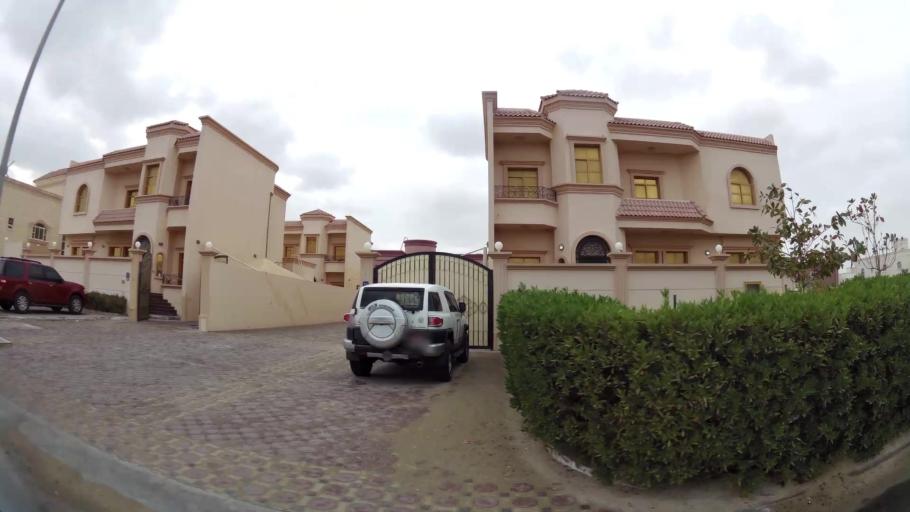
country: AE
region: Abu Dhabi
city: Abu Dhabi
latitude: 24.3459
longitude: 54.6319
